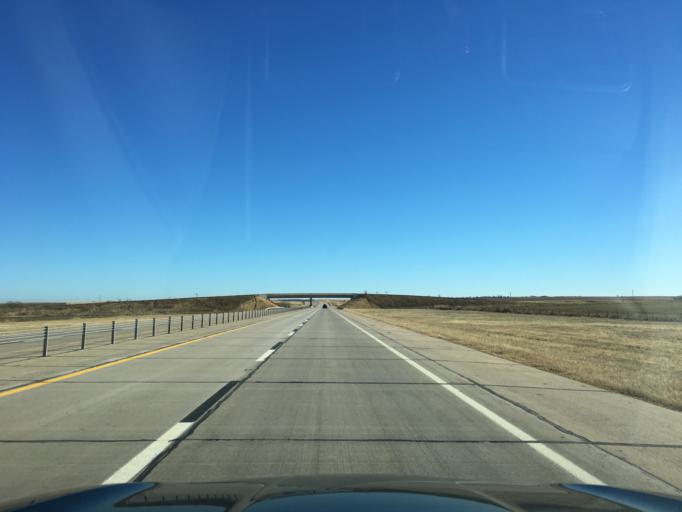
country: US
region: Oklahoma
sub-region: Noble County
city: Perry
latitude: 36.3975
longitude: -97.2328
